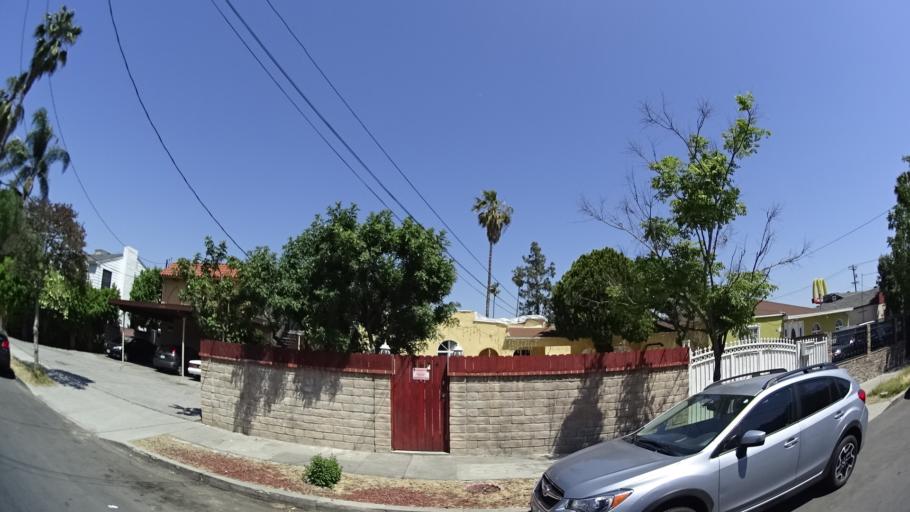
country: US
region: California
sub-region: Los Angeles County
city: North Hollywood
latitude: 34.1730
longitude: -118.3732
